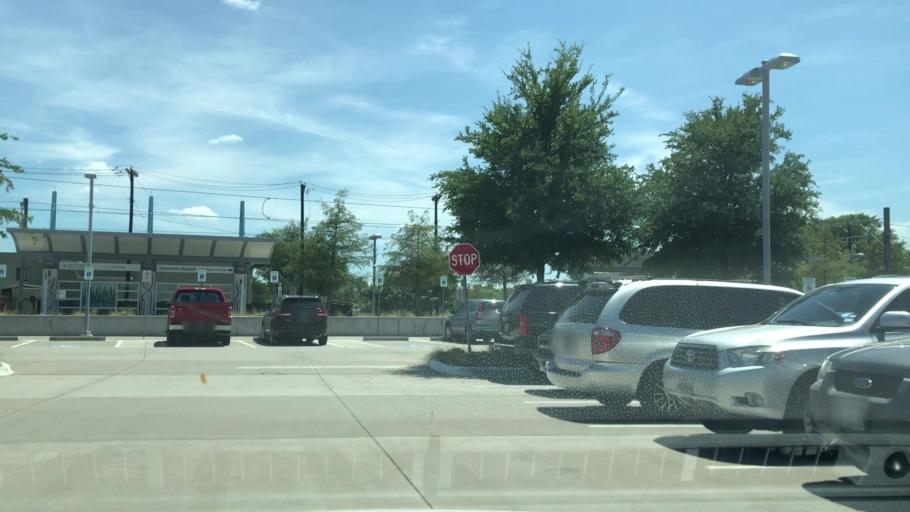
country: US
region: Texas
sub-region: Dallas County
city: Rowlett
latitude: 32.9048
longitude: -96.5633
